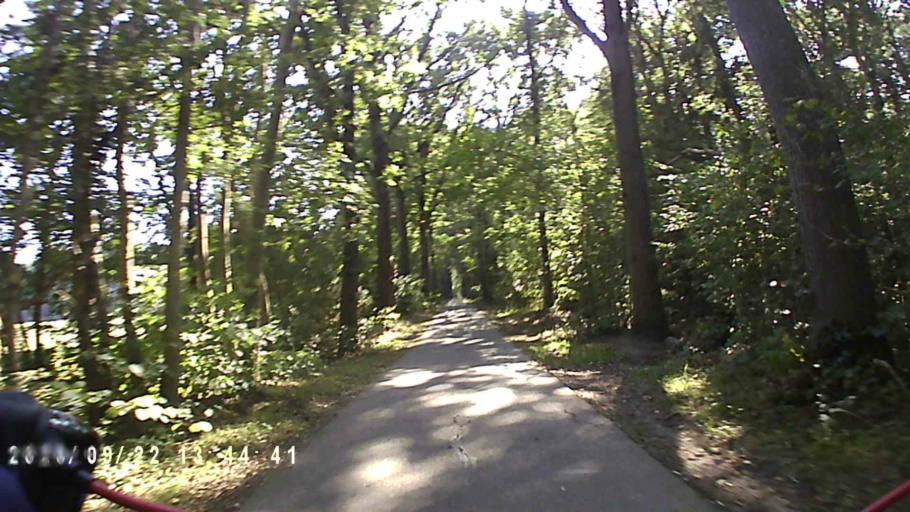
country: NL
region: Groningen
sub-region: Gemeente Leek
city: Leek
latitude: 53.1491
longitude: 6.4056
